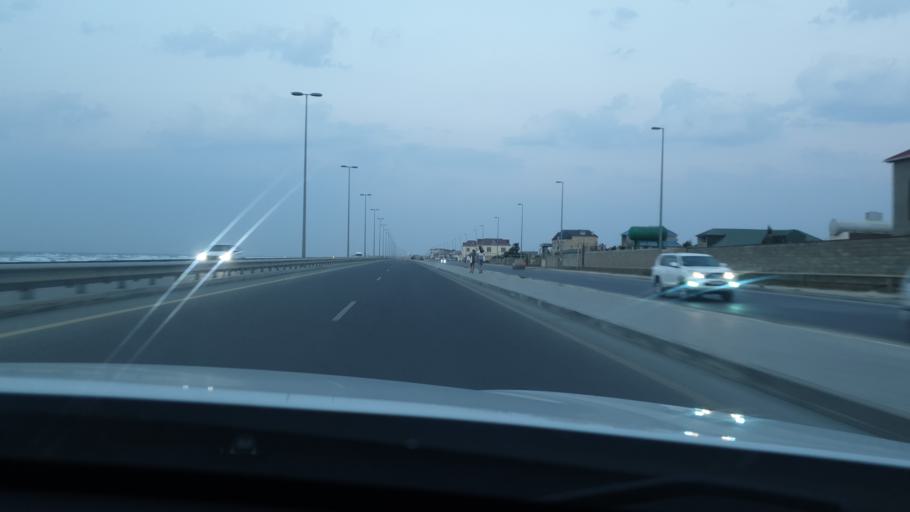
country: AZ
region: Baki
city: Bilajer
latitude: 40.5863
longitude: 50.0337
